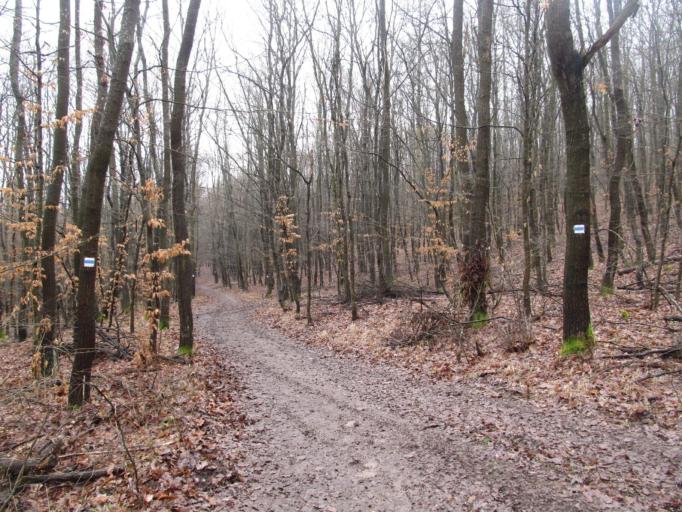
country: HU
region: Pest
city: Vac
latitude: 47.8488
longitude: 19.1106
